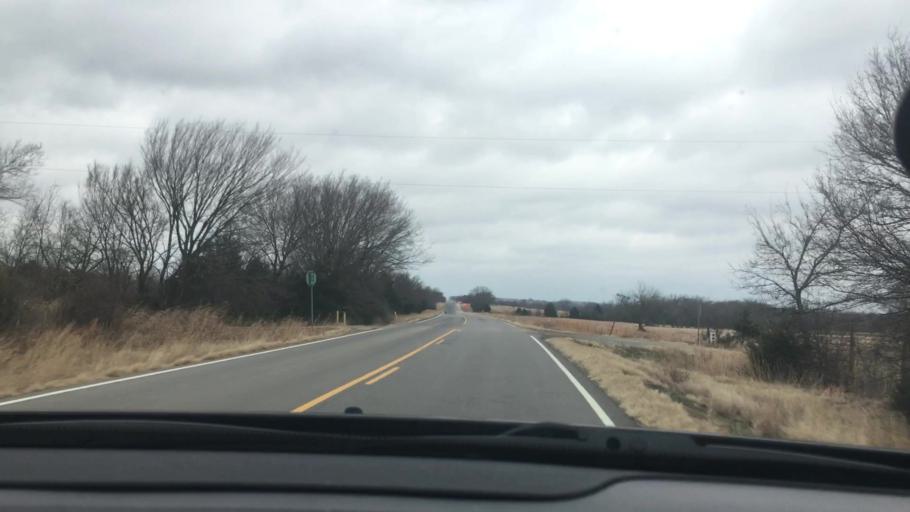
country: US
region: Oklahoma
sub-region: Atoka County
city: Atoka
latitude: 34.3749
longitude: -96.1973
